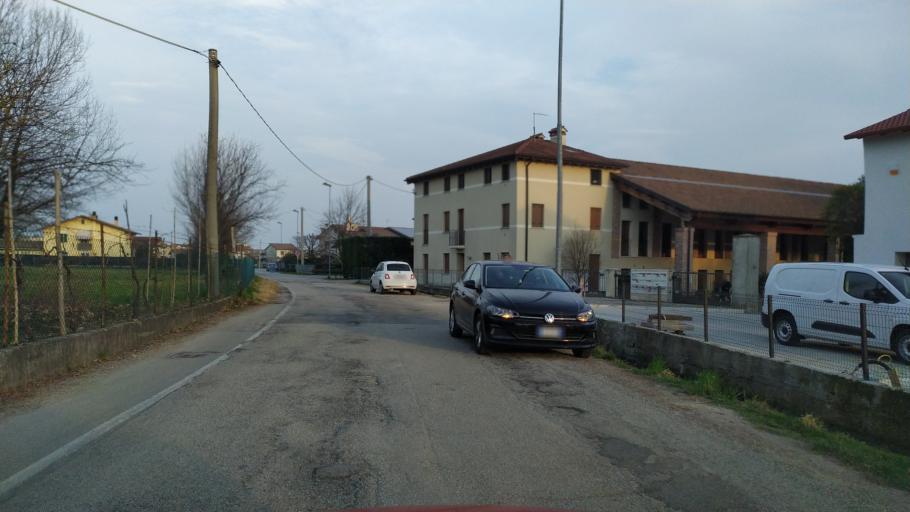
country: IT
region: Veneto
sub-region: Provincia di Vicenza
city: Marano Vicentino
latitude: 45.6902
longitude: 11.4361
